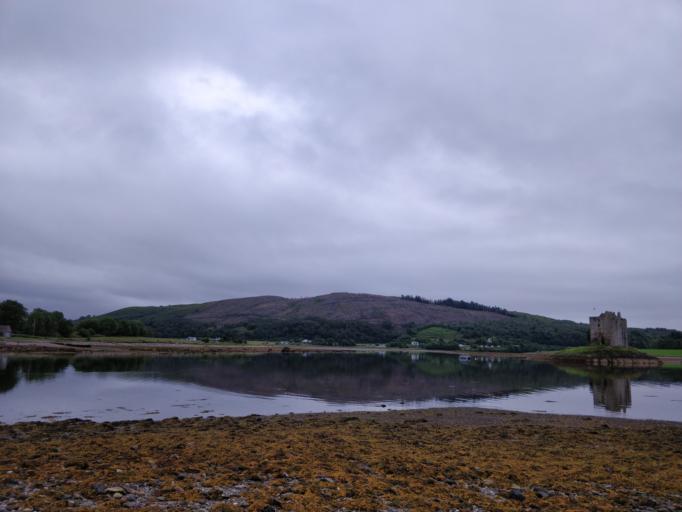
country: GB
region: Scotland
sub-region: Argyll and Bute
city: Oban
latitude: 56.5745
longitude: -5.3855
